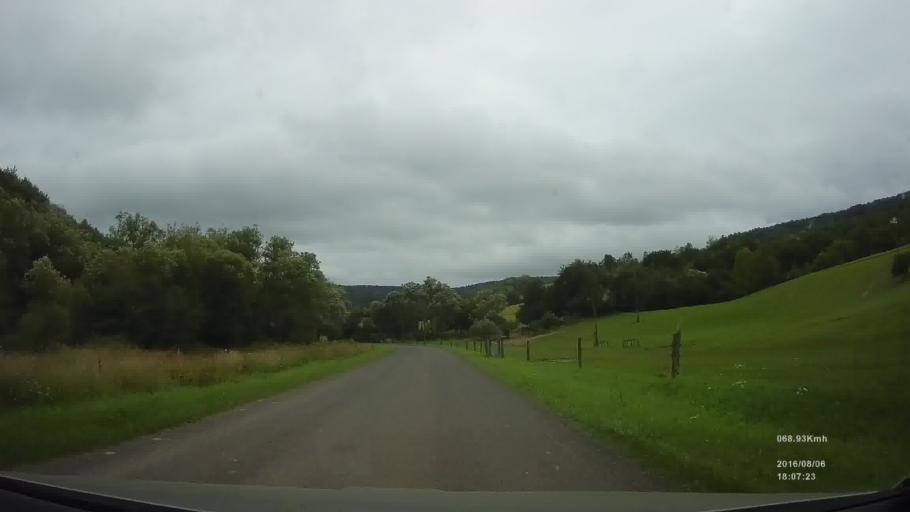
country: SK
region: Presovsky
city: Svidnik
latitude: 49.3963
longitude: 21.5691
